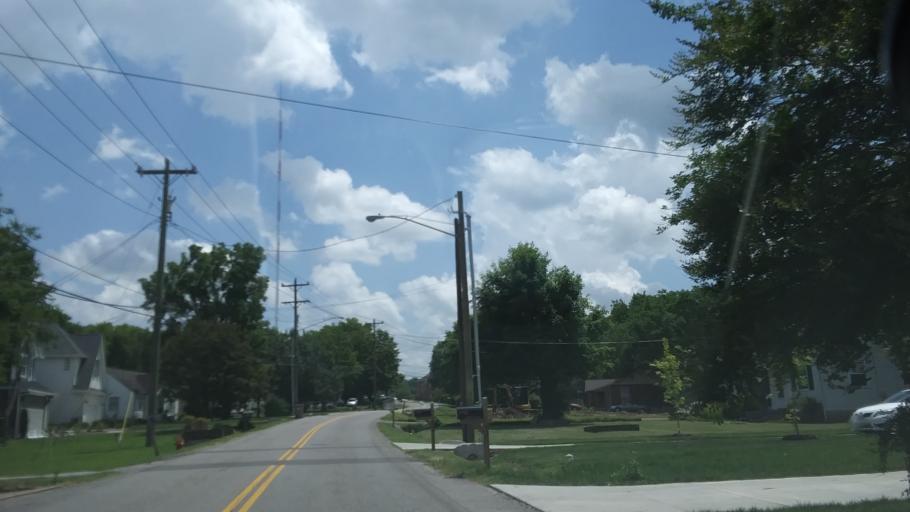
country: US
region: Tennessee
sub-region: Davidson County
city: Belle Meade
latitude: 36.1482
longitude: -86.8726
